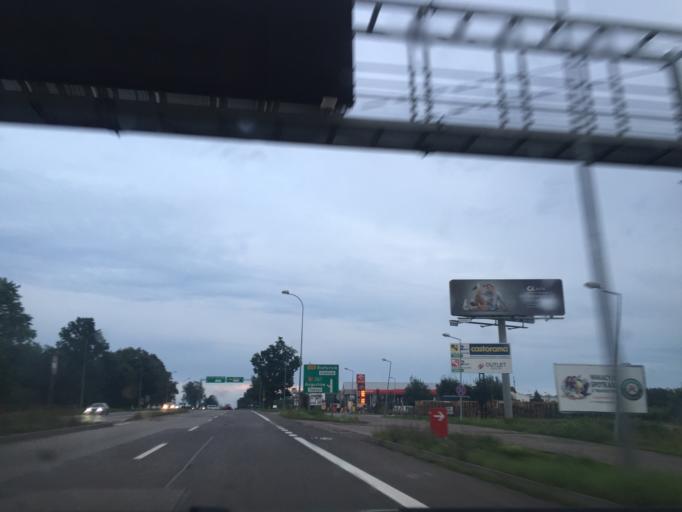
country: PL
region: Podlasie
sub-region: Powiat bialostocki
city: Choroszcz
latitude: 53.1491
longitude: 23.0557
